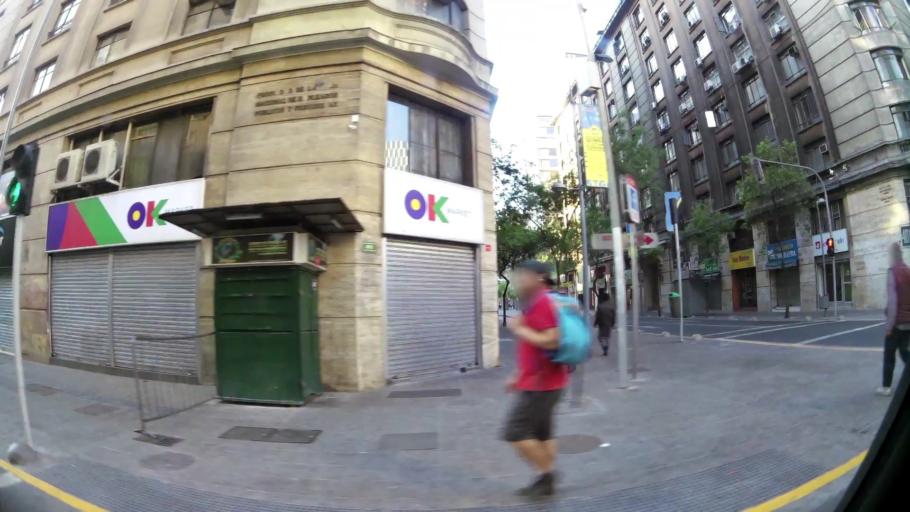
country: CL
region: Santiago Metropolitan
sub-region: Provincia de Santiago
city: Santiago
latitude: -33.4382
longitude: -70.6484
